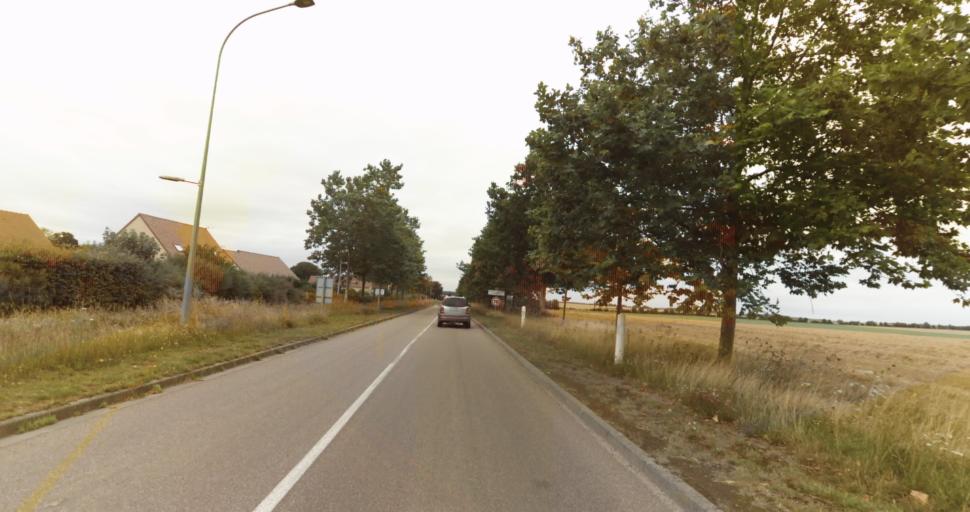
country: FR
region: Haute-Normandie
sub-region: Departement de l'Eure
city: Marcilly-sur-Eure
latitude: 48.9105
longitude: 1.2823
